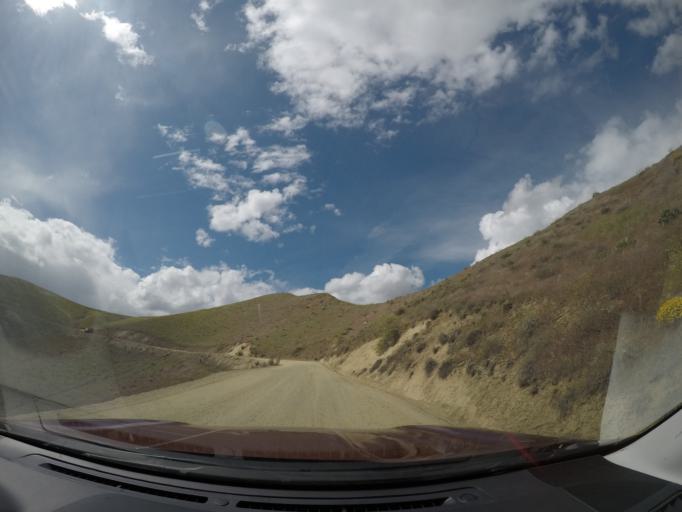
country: US
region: Washington
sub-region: Chelan County
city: West Wenatchee
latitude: 47.4632
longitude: -120.3731
